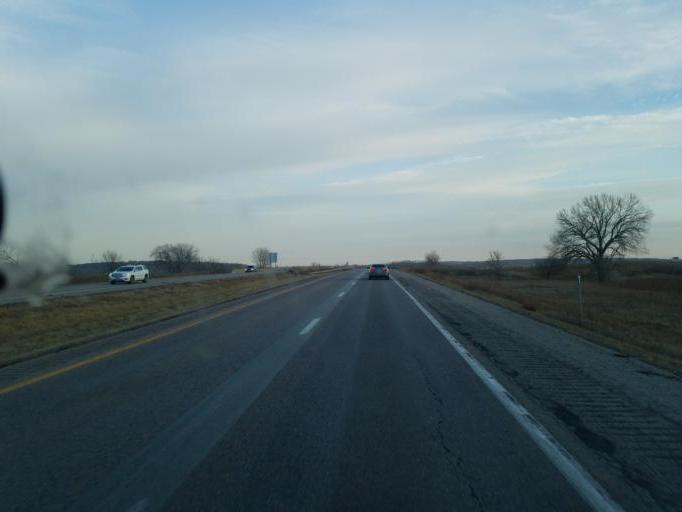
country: US
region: Iowa
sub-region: Harrison County
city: Missouri Valley
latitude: 41.5749
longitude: -95.9298
